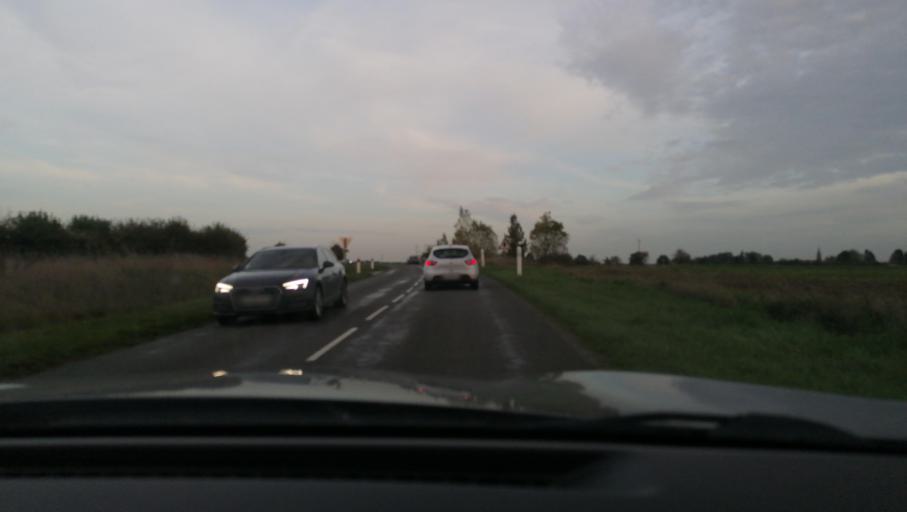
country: FR
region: Picardie
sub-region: Departement de la Somme
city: Picquigny
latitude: 49.8902
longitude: 2.1333
